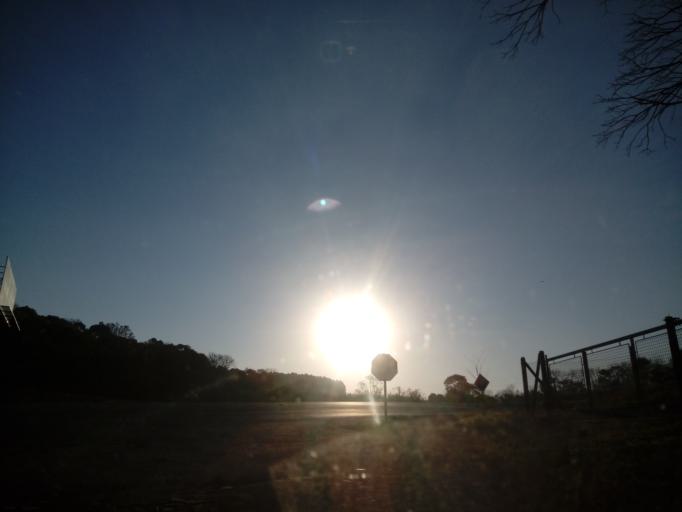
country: BR
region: Santa Catarina
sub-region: Chapeco
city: Chapeco
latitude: -27.2316
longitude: -52.6845
